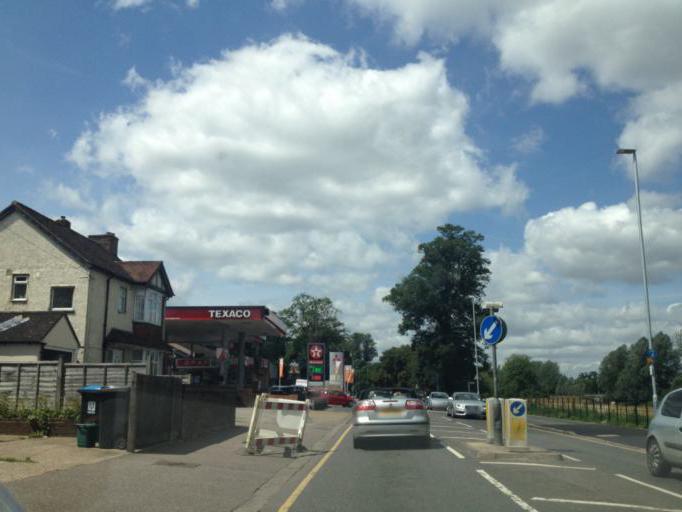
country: GB
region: England
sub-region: Hertfordshire
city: Hemel Hempstead
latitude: 51.7432
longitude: -0.4872
